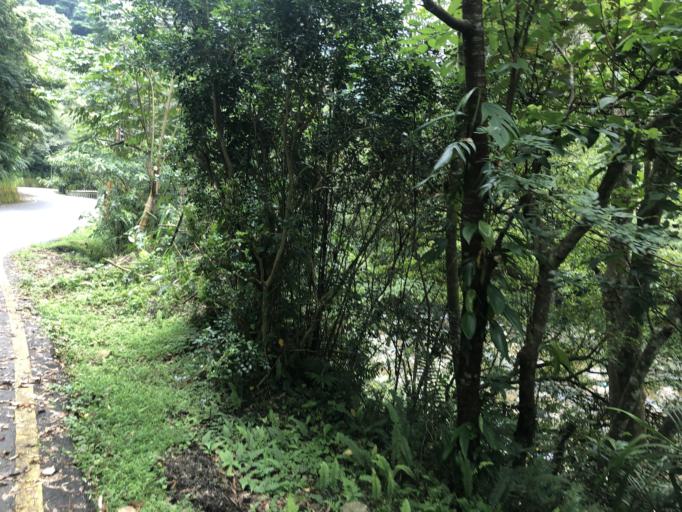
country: TW
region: Taipei
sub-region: Taipei
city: Banqiao
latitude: 24.8467
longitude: 121.4551
